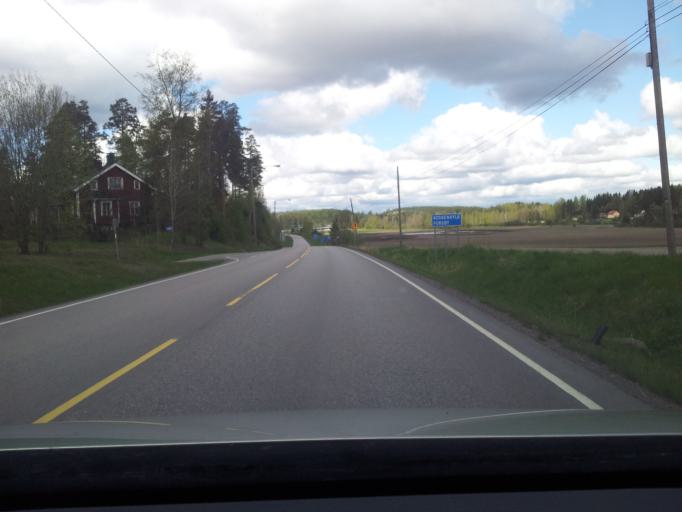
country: FI
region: Uusimaa
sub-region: Loviisa
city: Perna
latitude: 60.4988
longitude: 25.9578
